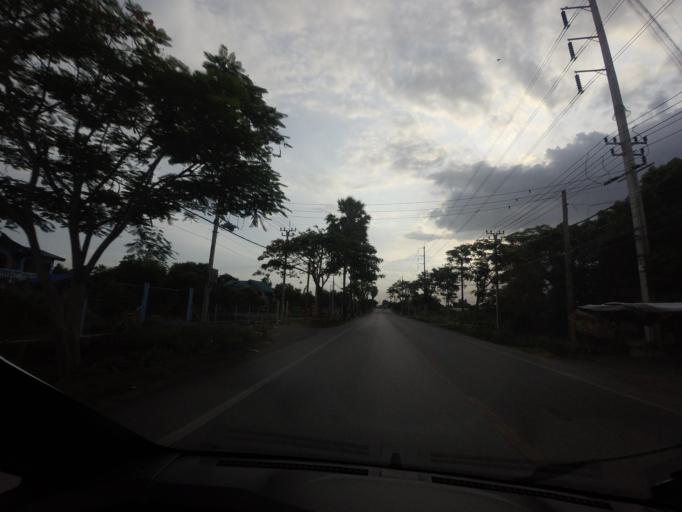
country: TH
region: Bangkok
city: Nong Chok
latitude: 13.8574
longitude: 100.8327
